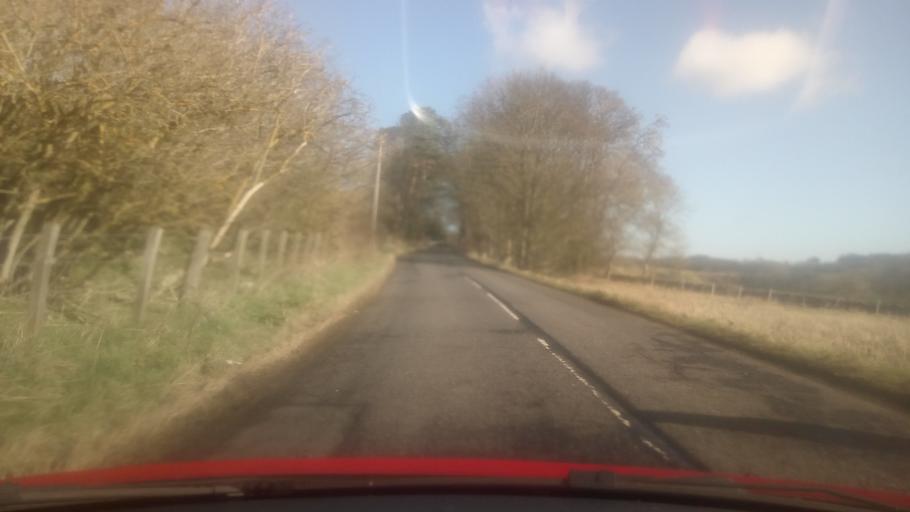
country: GB
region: Scotland
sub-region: The Scottish Borders
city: Selkirk
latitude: 55.5543
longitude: -2.8491
